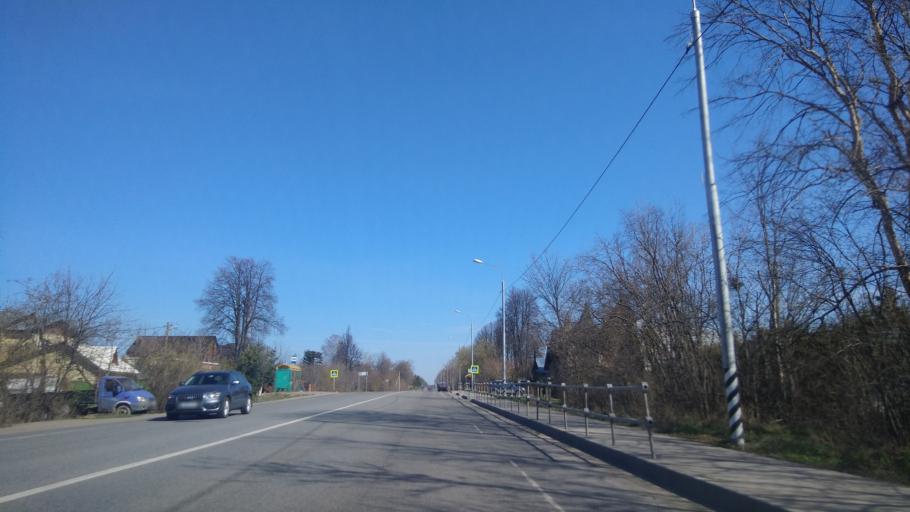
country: RU
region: Moskovskaya
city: Pushkino
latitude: 56.0212
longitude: 37.8715
